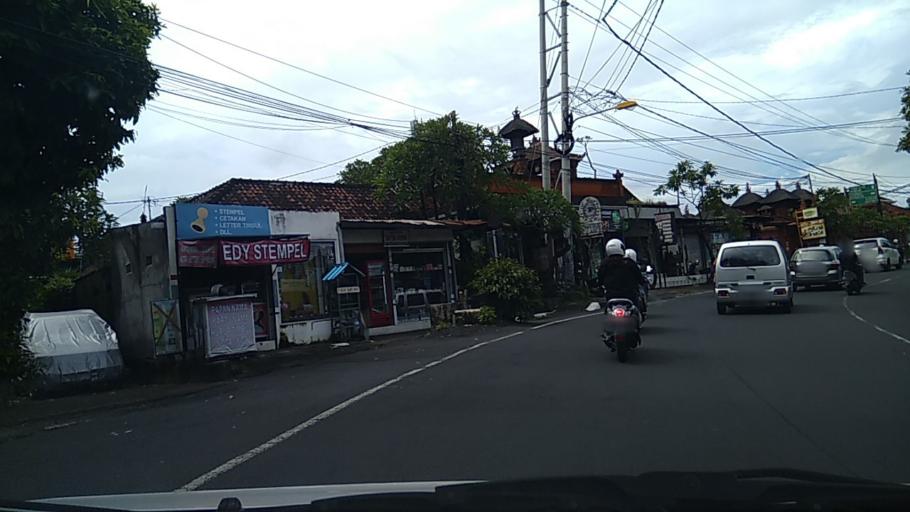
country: ID
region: Bali
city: Dajan Tangluk
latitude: -8.6459
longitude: 115.2459
